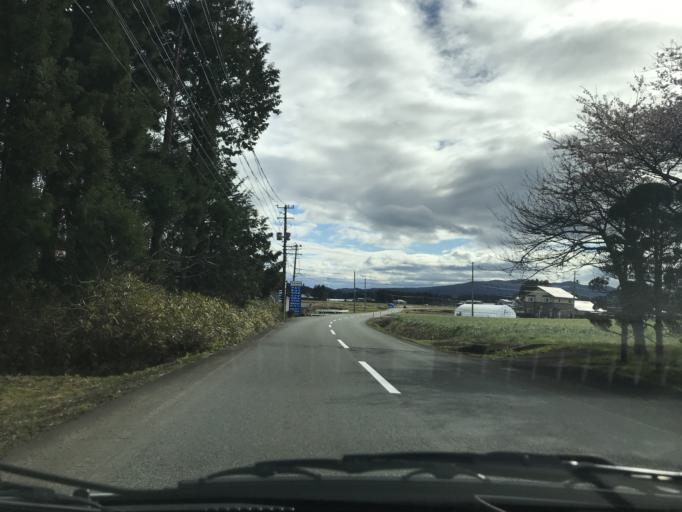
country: JP
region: Iwate
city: Mizusawa
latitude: 39.1104
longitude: 141.0670
